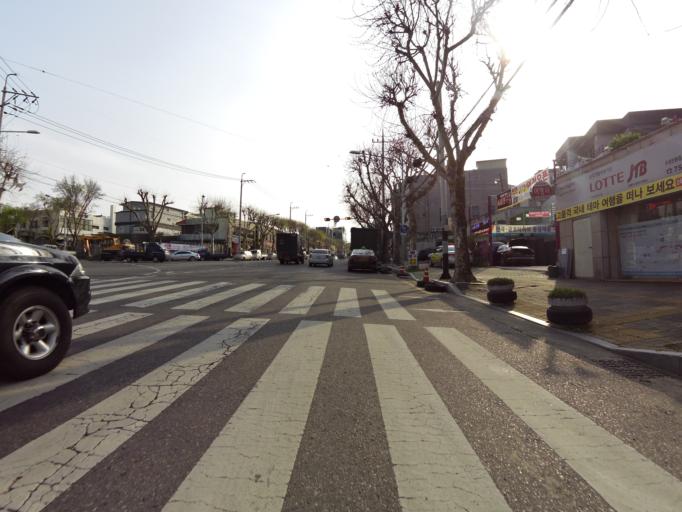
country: KR
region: Daegu
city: Daegu
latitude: 35.8673
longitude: 128.6448
